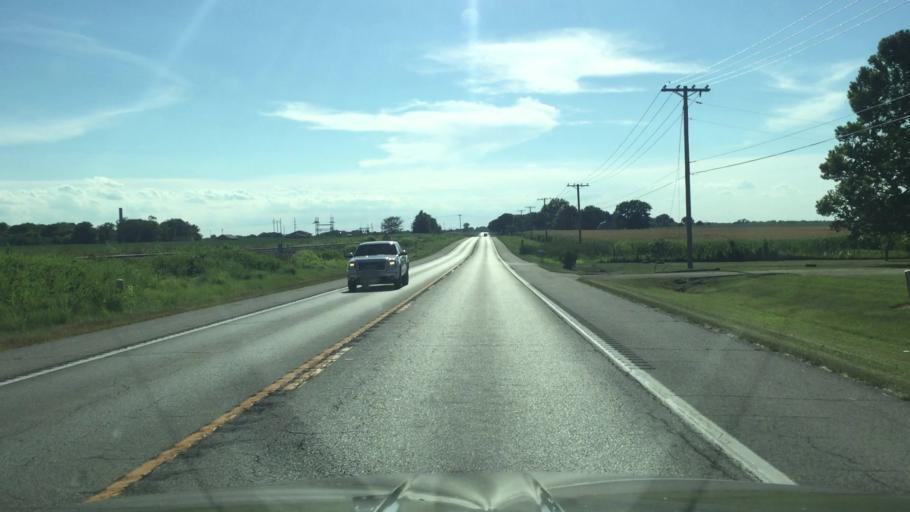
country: US
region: Missouri
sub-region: Pettis County
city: Sedalia
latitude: 38.6947
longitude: -93.1439
